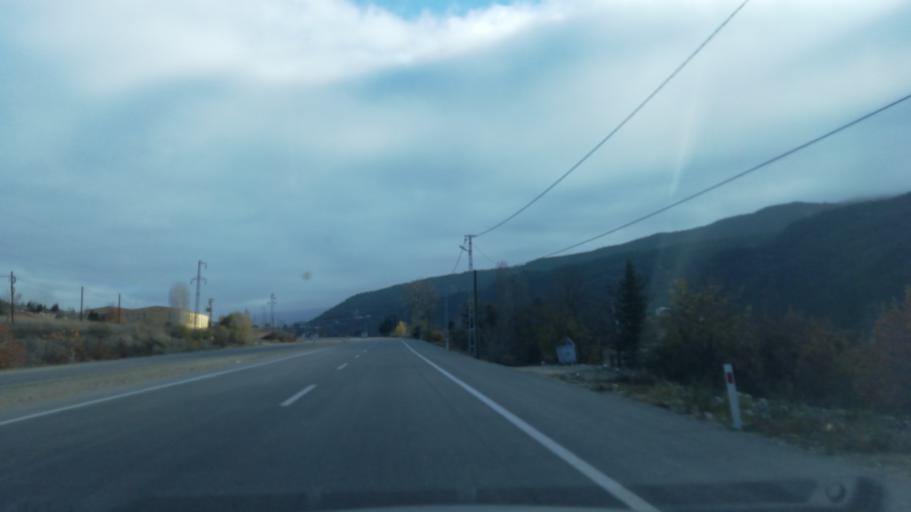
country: TR
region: Karabuk
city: Safranbolu
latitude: 41.2173
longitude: 32.7497
